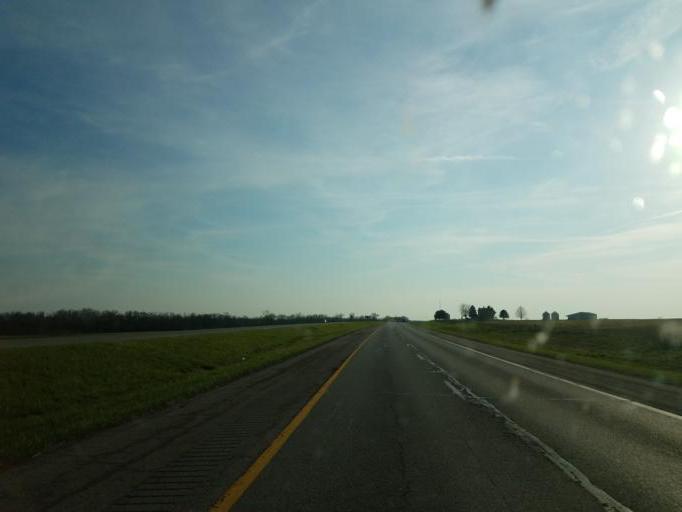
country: US
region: Ohio
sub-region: Warren County
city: Waynesville
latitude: 39.4632
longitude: -83.9842
